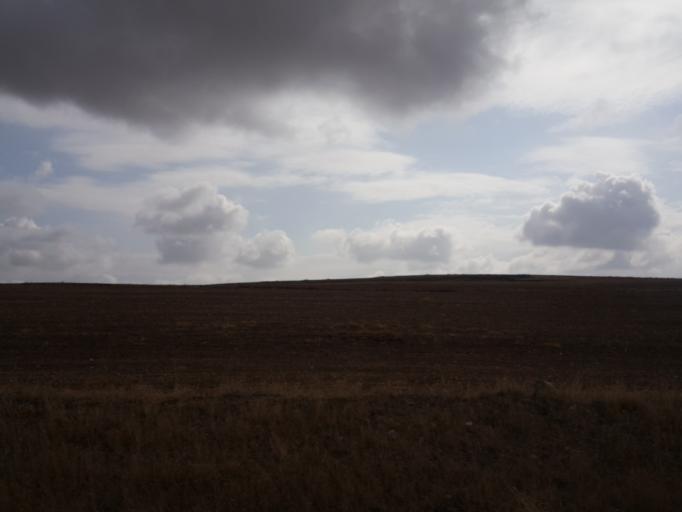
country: TR
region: Kirikkale
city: Keskin
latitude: 39.6428
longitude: 33.6167
